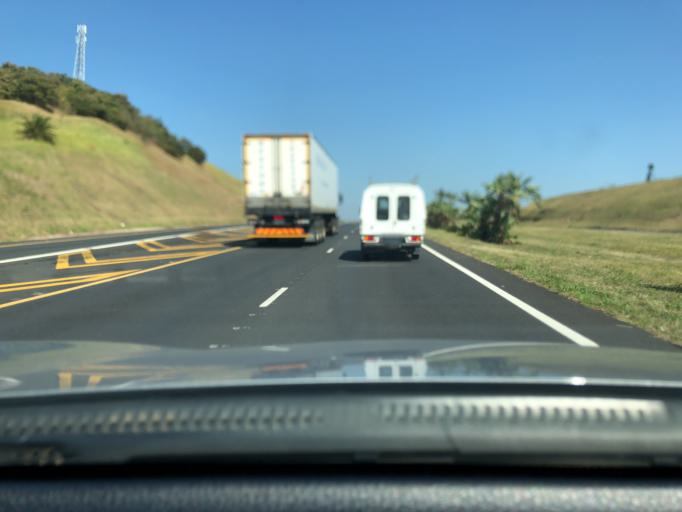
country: ZA
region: KwaZulu-Natal
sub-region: Ugu District Municipality
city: Scottburgh
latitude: -30.2659
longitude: 30.7569
